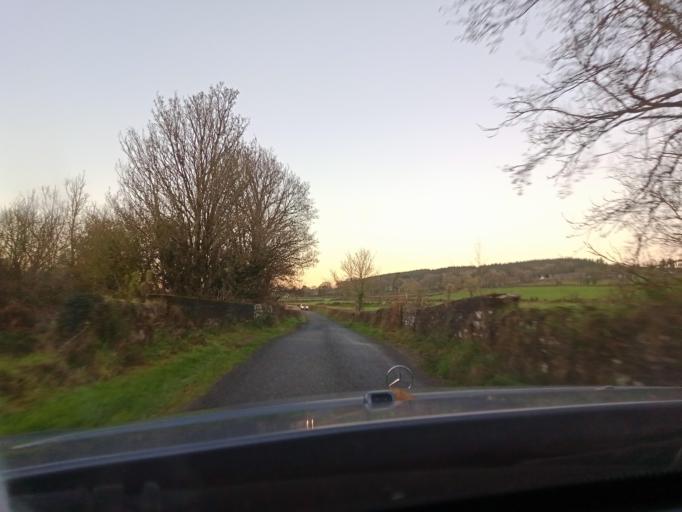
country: IE
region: Leinster
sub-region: Kilkenny
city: Thomastown
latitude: 52.4382
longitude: -7.1079
